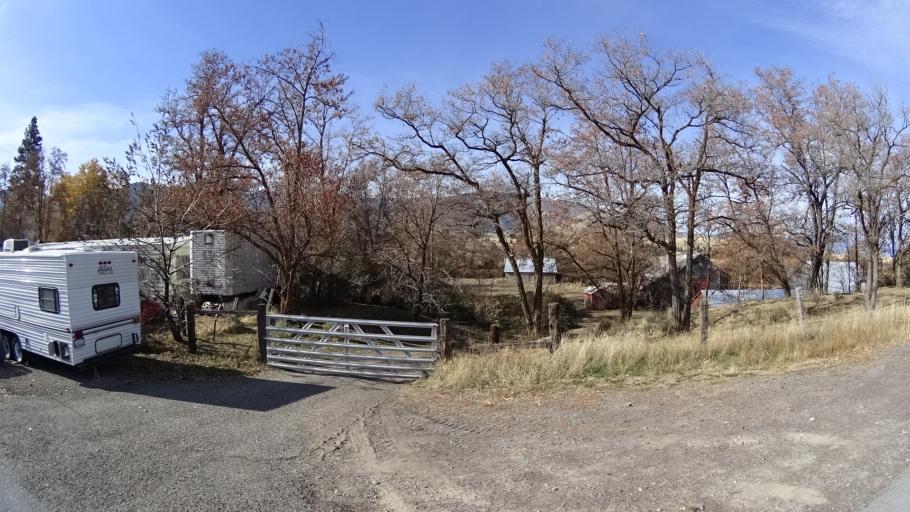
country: US
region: California
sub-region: Siskiyou County
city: Weed
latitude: 41.4486
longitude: -122.4304
